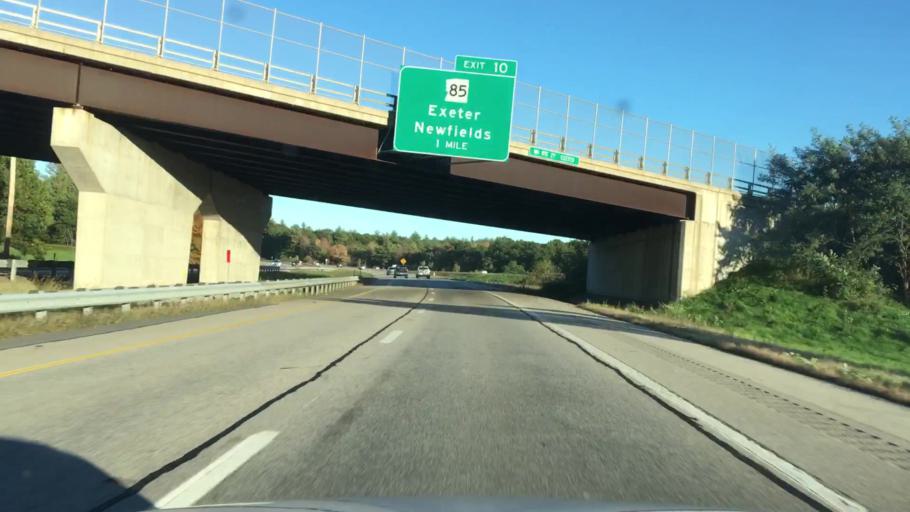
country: US
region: New Hampshire
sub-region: Rockingham County
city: Exeter
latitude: 43.0015
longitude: -70.9765
